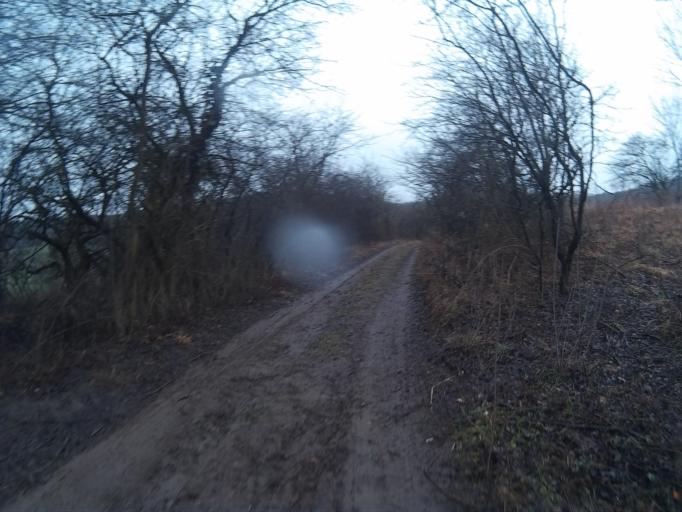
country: HU
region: Komarom-Esztergom
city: Nyergesujfalu
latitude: 47.7238
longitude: 18.5869
